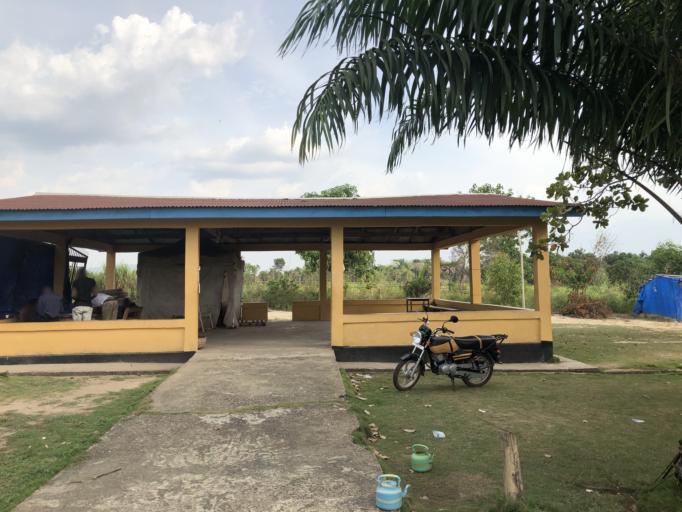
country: SL
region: Northern Province
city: Yonibana
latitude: 8.4584
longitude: -12.2469
